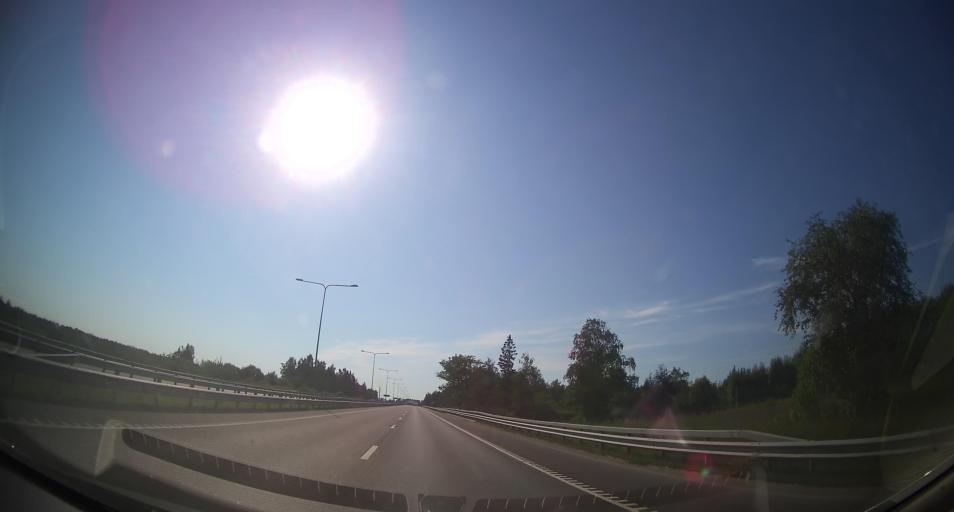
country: EE
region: Harju
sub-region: Maardu linn
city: Maardu
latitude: 59.4532
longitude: 25.0359
